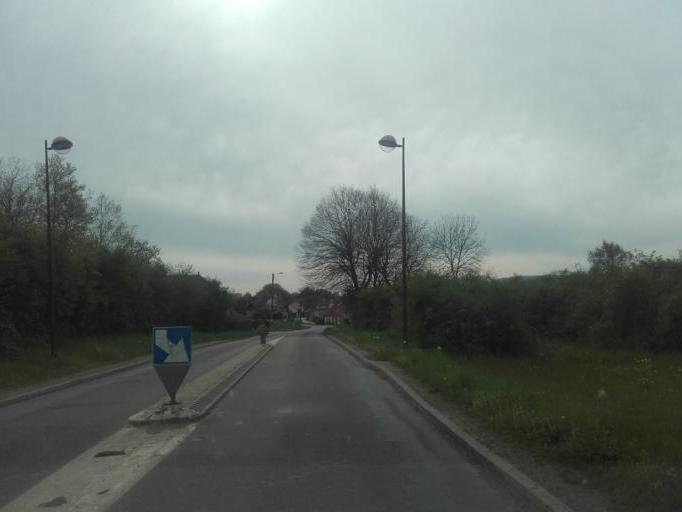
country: FR
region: Bourgogne
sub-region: Departement de Saone-et-Loire
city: Demigny
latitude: 46.9170
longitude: 4.8066
